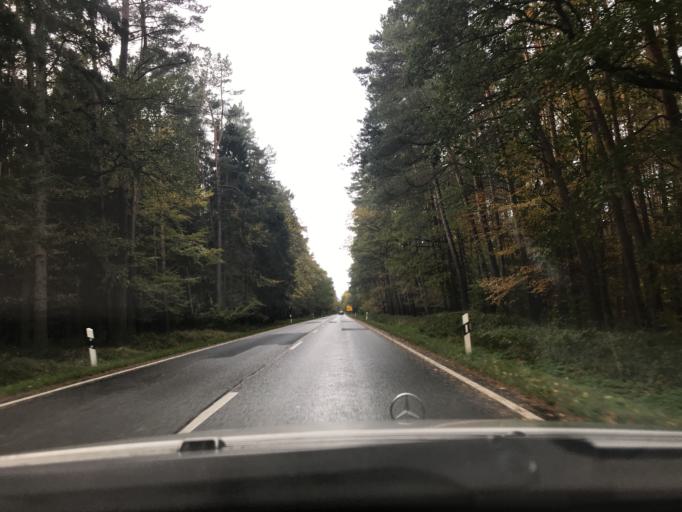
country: DE
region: Mecklenburg-Vorpommern
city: Wolgast
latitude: 54.0223
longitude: 13.6718
